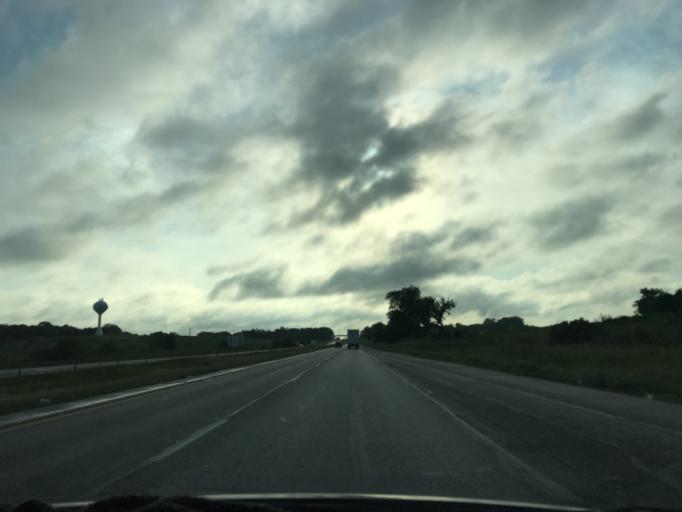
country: US
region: Iowa
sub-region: Johnson County
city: Tiffin
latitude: 41.6937
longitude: -91.6596
